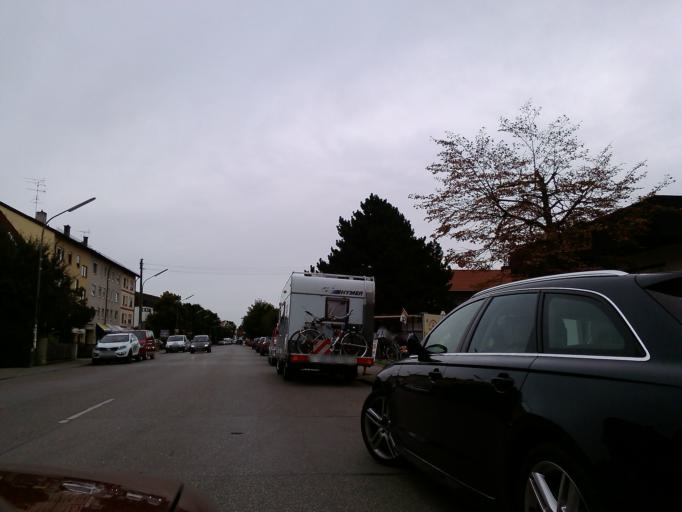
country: DE
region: Bavaria
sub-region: Upper Bavaria
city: Gilching
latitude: 48.1105
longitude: 11.2980
